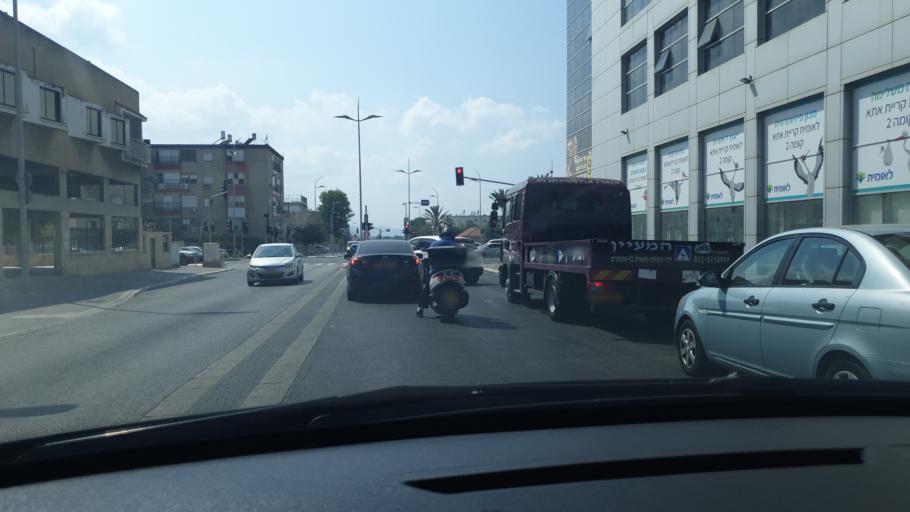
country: IL
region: Haifa
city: Qiryat Ata
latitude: 32.8124
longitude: 35.1057
